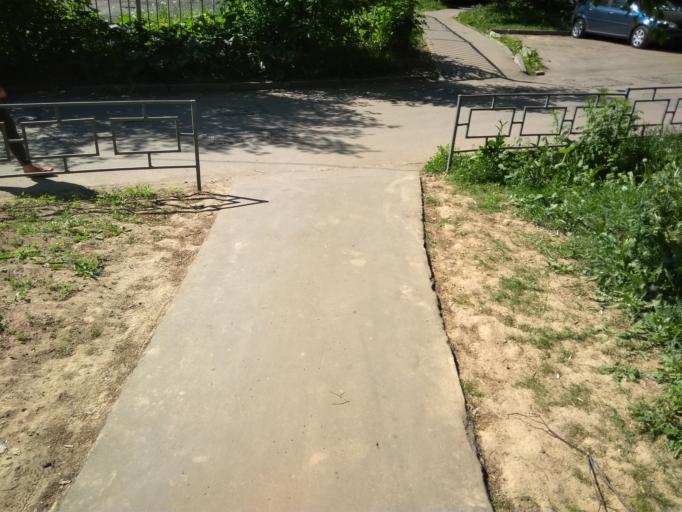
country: RU
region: Moskovskaya
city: Troitsk
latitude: 55.4860
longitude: 37.2999
